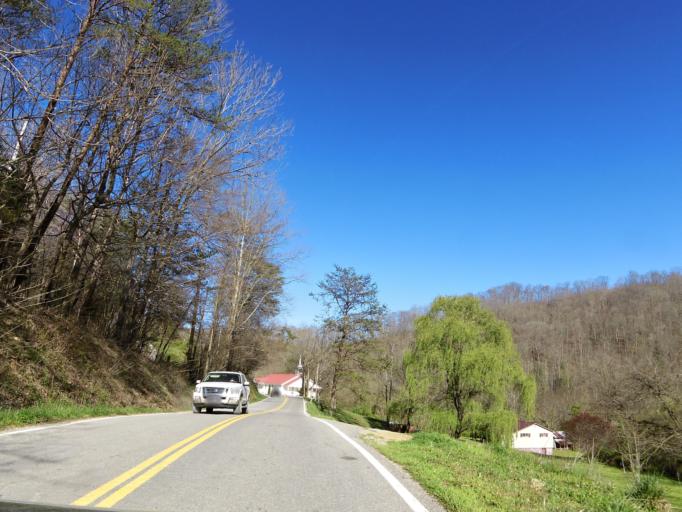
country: US
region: Tennessee
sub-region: Scott County
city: Huntsville
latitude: 36.3268
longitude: -84.3705
